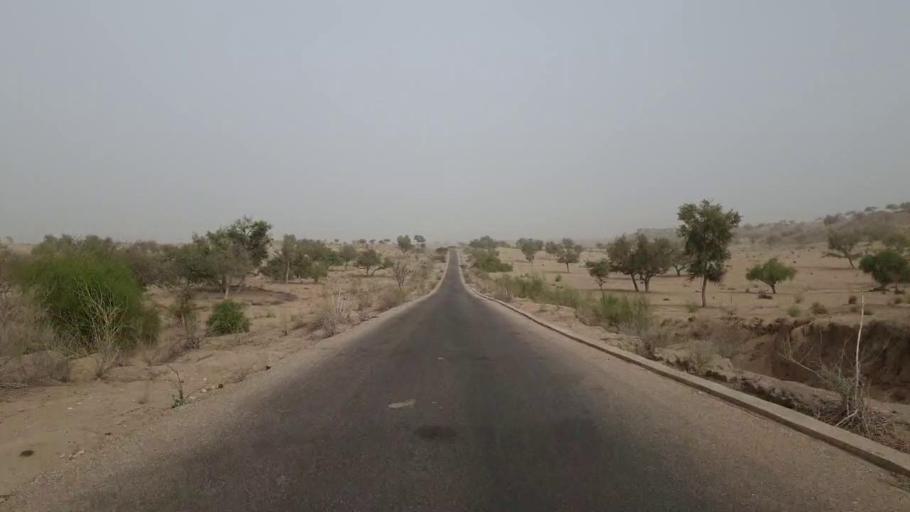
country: PK
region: Sindh
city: Islamkot
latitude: 24.5857
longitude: 70.2958
